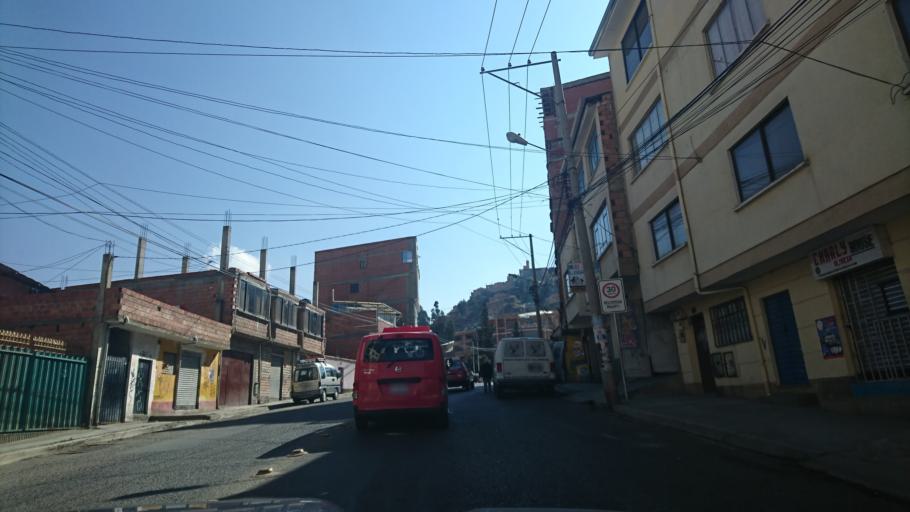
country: BO
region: La Paz
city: La Paz
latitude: -16.4848
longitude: -68.1173
